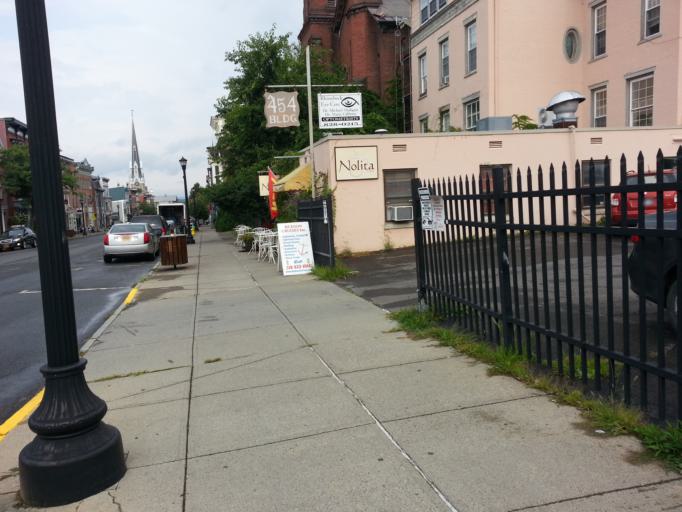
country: US
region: New York
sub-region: Columbia County
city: Hudson
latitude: 42.2497
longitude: -73.7867
